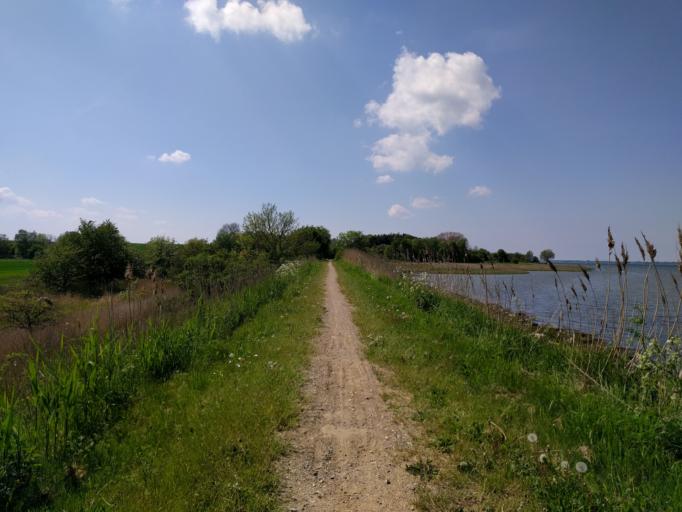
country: DK
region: Zealand
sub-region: Guldborgsund Kommune
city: Stubbekobing
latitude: 54.8882
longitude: 12.0972
